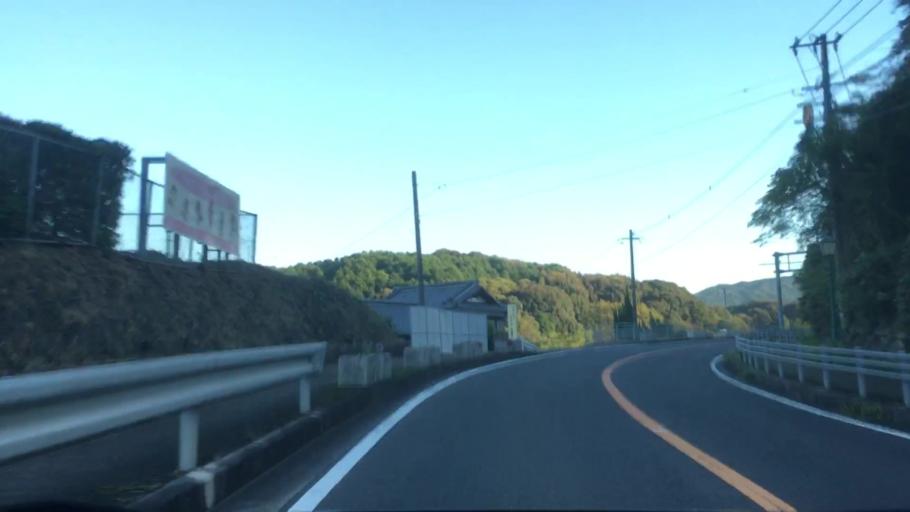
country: JP
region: Nagasaki
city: Sasebo
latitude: 33.0002
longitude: 129.7318
